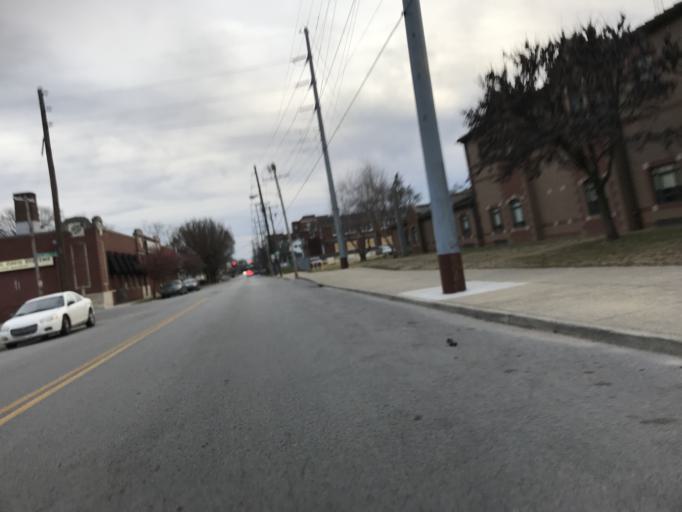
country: US
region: Kentucky
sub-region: Jefferson County
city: Louisville
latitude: 38.2399
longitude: -85.7507
